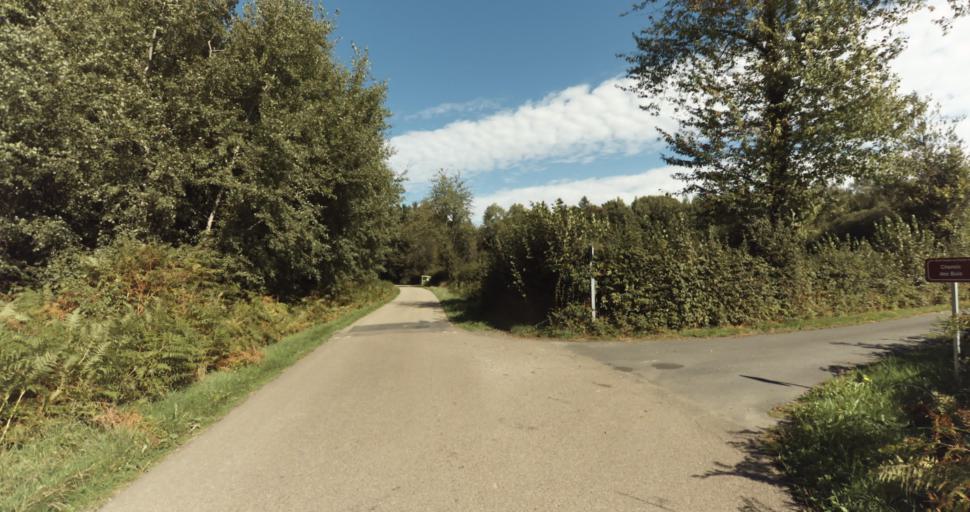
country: FR
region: Lower Normandy
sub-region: Departement de l'Orne
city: Gace
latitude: 48.7925
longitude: 0.2338
